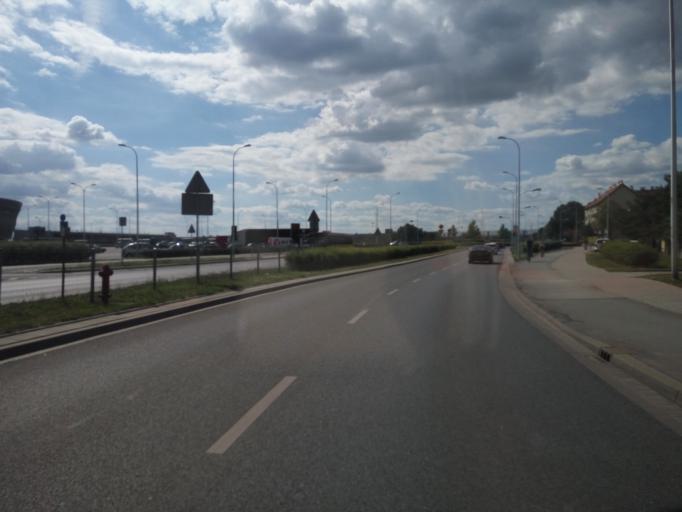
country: PL
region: Lower Silesian Voivodeship
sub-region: Powiat trzebnicki
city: Psary
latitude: 51.1439
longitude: 16.9507
